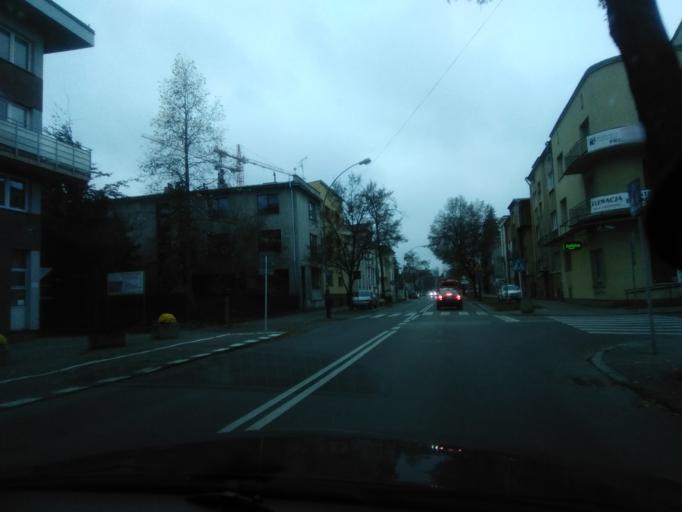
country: PL
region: Subcarpathian Voivodeship
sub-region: Rzeszow
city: Rzeszow
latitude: 50.0339
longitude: 22.0072
